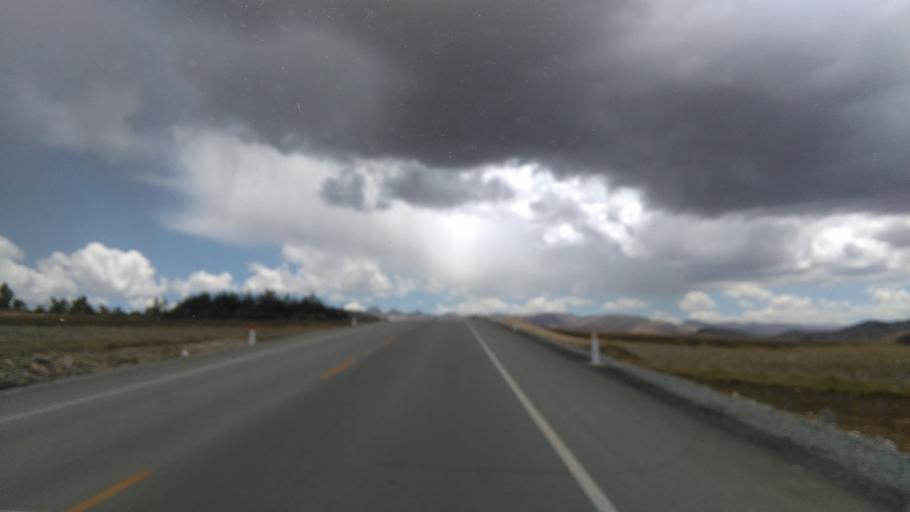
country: PE
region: Apurimac
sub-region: Provincia de Andahuaylas
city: San Jeronimo
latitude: -13.7216
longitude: -73.3504
